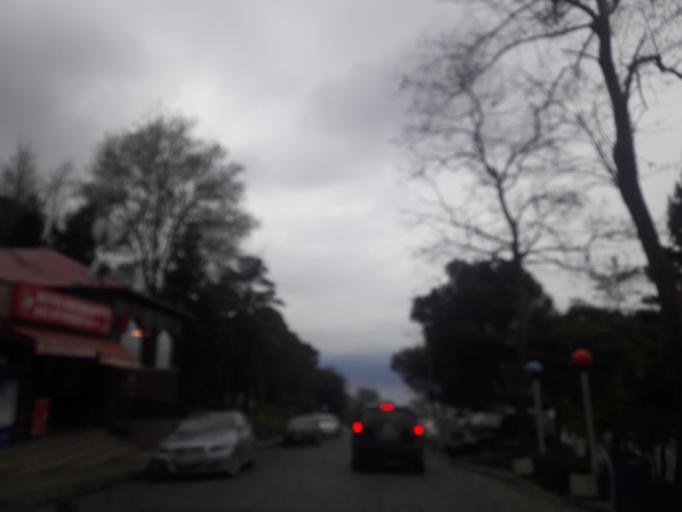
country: TR
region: Trabzon
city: Trabzon
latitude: 40.9974
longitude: 39.7330
